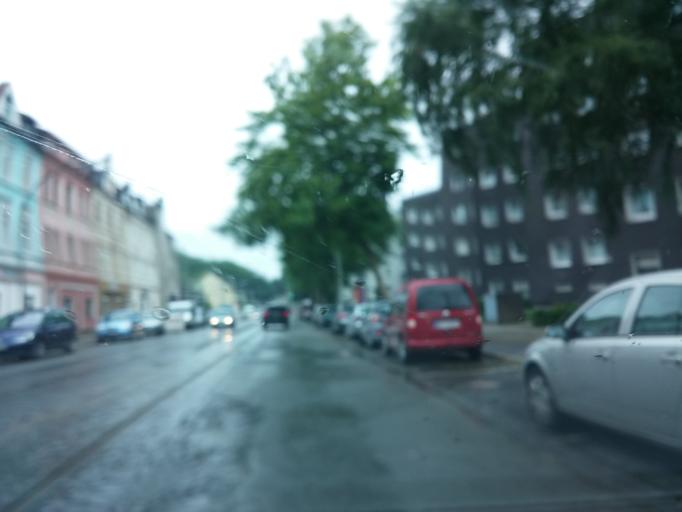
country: DE
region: North Rhine-Westphalia
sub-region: Regierungsbezirk Munster
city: Gladbeck
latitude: 51.5616
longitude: 7.0465
